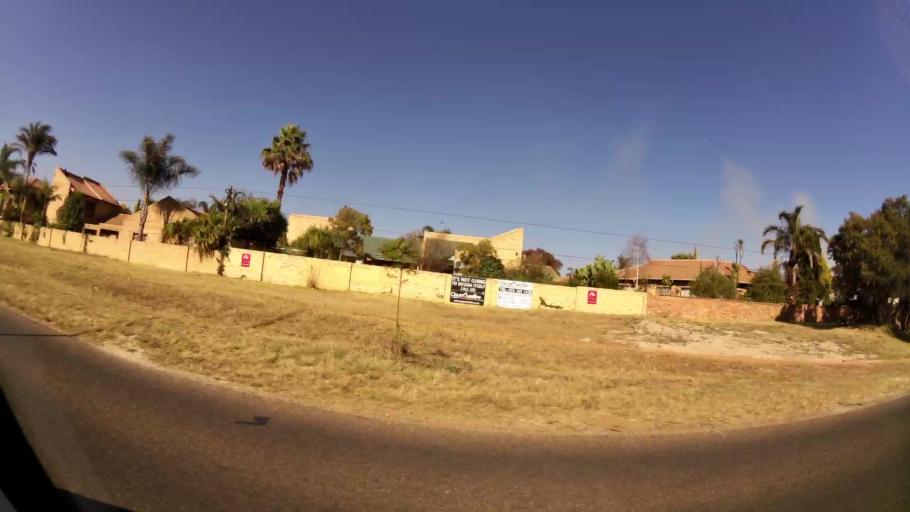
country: ZA
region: Gauteng
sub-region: City of Tshwane Metropolitan Municipality
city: Centurion
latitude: -25.8385
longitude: 28.2841
